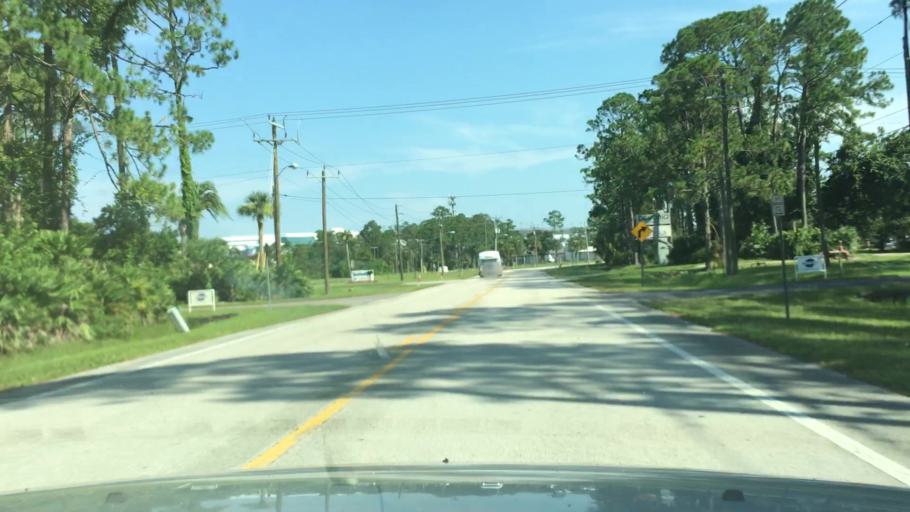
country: US
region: Florida
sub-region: Volusia County
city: Daytona Beach
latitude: 29.1952
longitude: -81.0798
